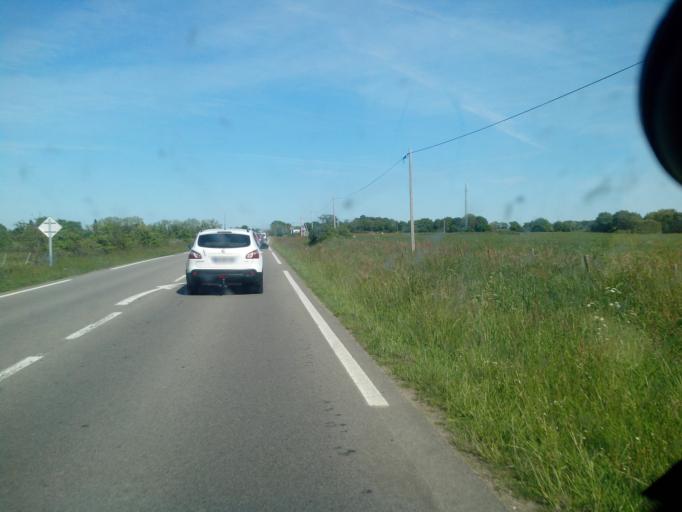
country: FR
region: Pays de la Loire
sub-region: Departement de la Loire-Atlantique
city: Arthon-en-Retz
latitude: 47.1113
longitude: -1.9812
